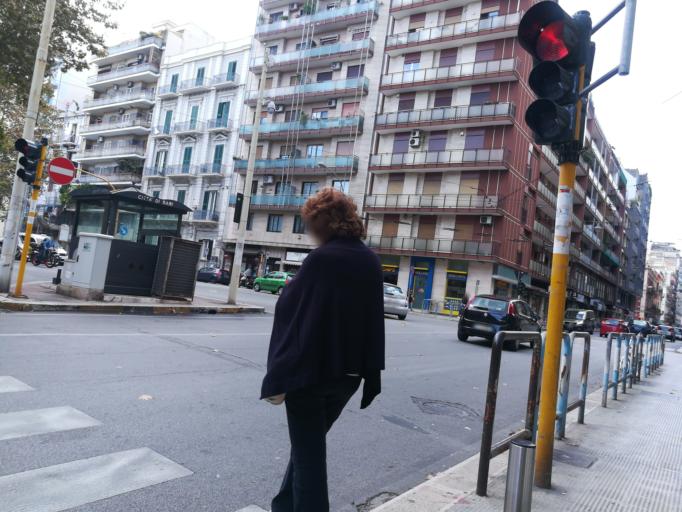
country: IT
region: Apulia
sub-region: Provincia di Bari
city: Bari
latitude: 41.1201
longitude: 16.8742
